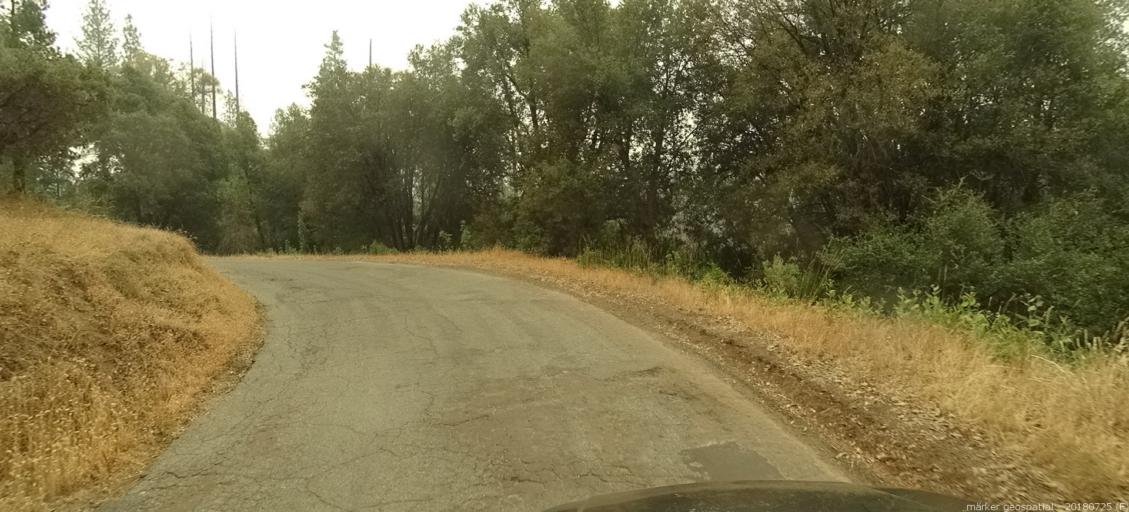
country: US
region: California
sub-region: Madera County
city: Oakhurst
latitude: 37.3625
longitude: -119.6046
